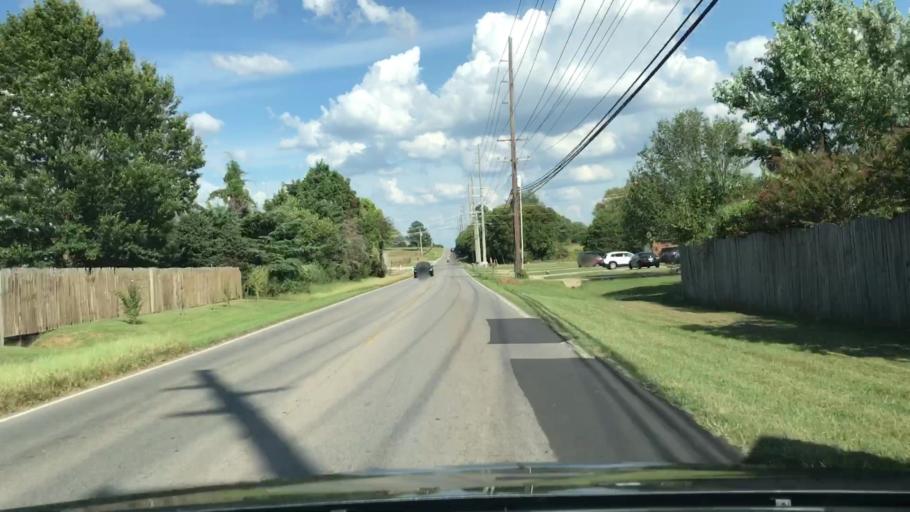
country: US
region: Alabama
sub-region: Madison County
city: Harvest
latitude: 34.8085
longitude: -86.7419
